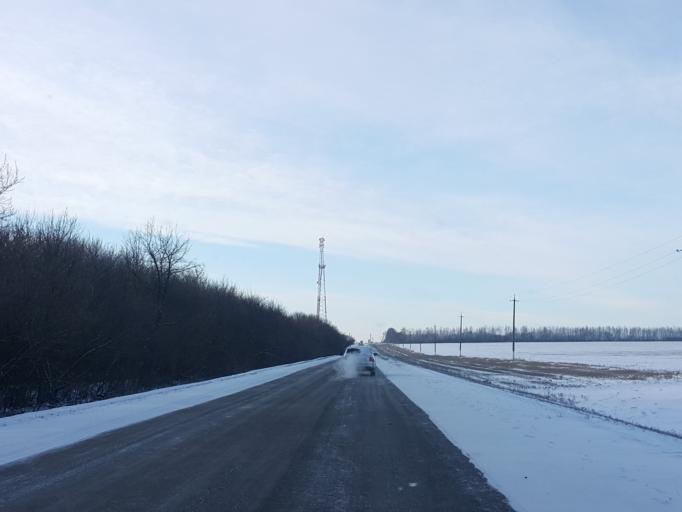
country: RU
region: Tambov
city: Znamenka
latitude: 52.4063
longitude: 41.4028
